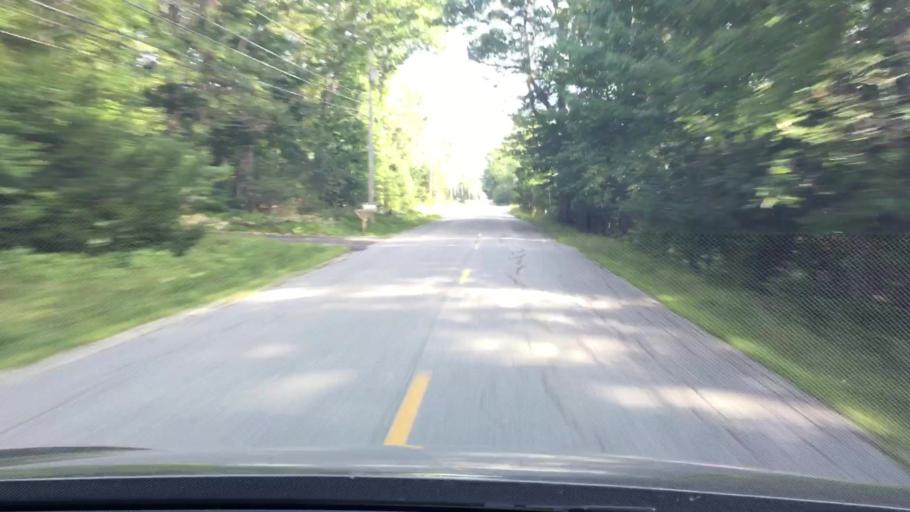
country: US
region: Maine
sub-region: Hancock County
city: Bucksport
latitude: 44.5392
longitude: -68.7950
